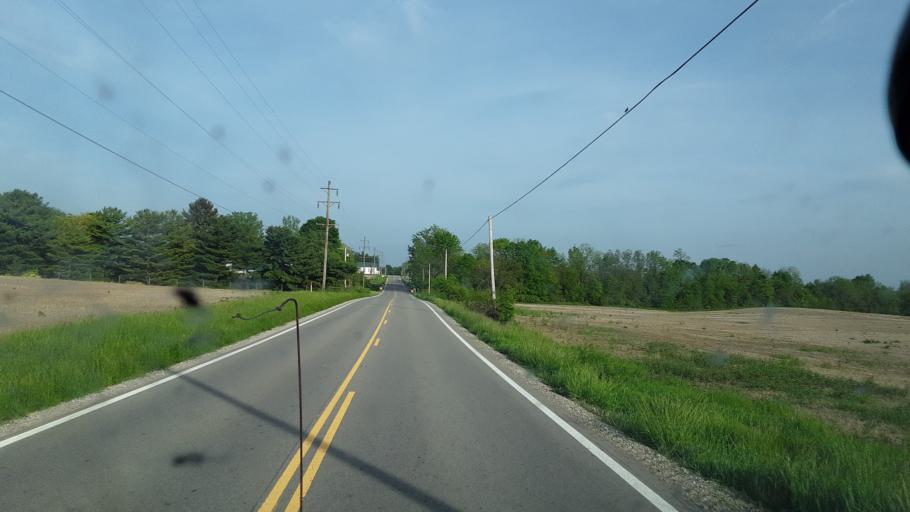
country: US
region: Ohio
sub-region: Ross County
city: Kingston
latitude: 39.5212
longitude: -82.8208
